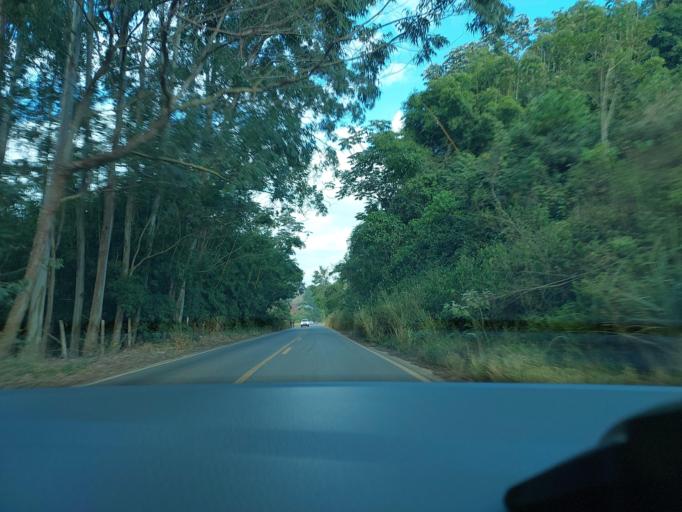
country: BR
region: Minas Gerais
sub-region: Vicosa
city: Vicosa
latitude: -20.8386
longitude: -42.6895
